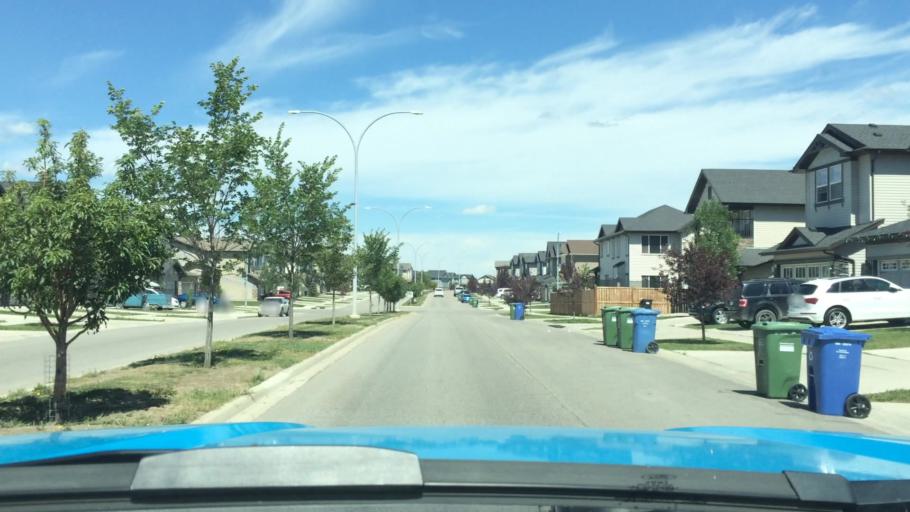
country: CA
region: Alberta
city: Calgary
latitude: 51.1767
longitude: -114.1538
